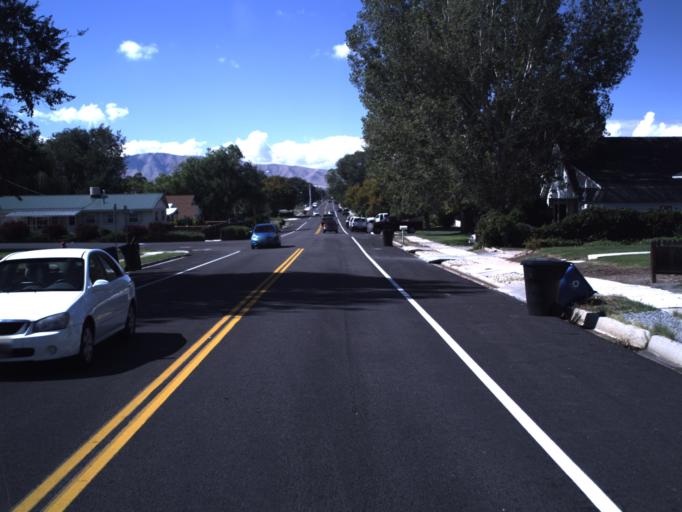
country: US
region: Utah
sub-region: Utah County
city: Spanish Fork
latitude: 40.1150
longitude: -111.6433
